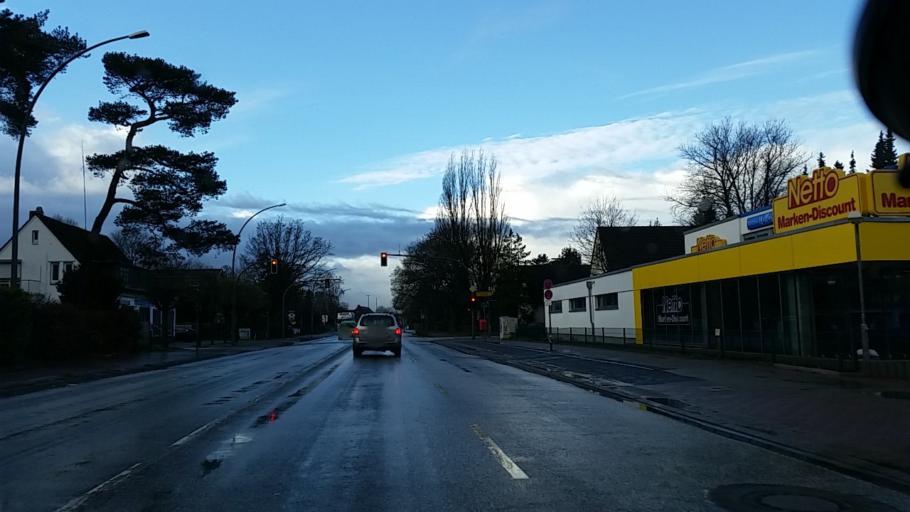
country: DE
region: Schleswig-Holstein
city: Halstenbek
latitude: 53.5981
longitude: 9.8590
